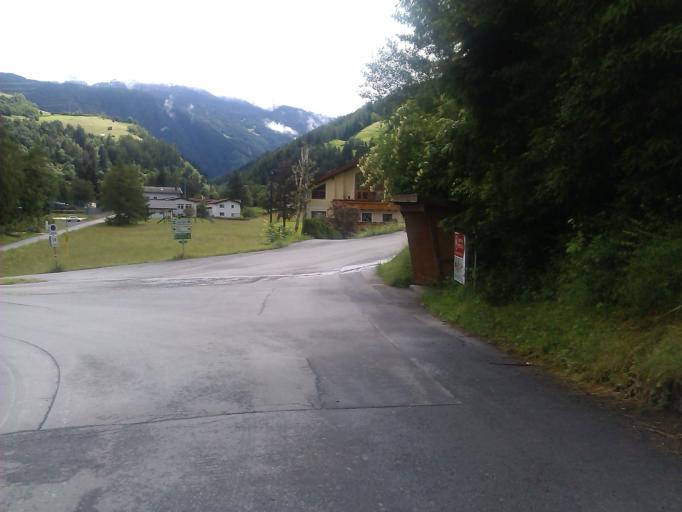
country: AT
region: Tyrol
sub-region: Politischer Bezirk Landeck
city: Zams
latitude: 47.1168
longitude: 10.6059
